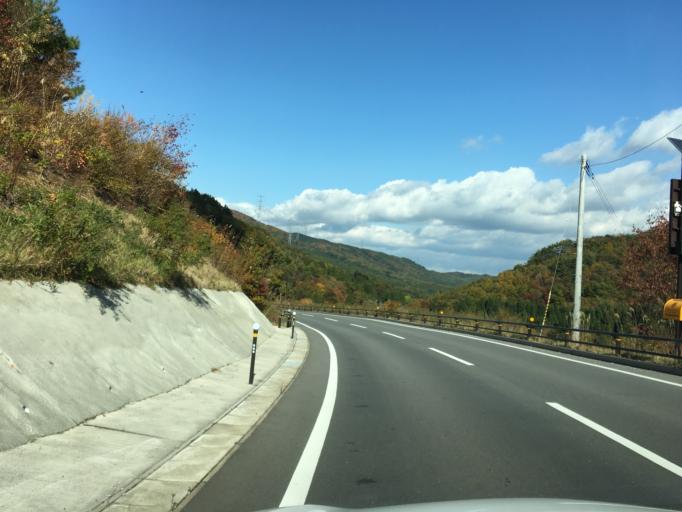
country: JP
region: Fukushima
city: Funehikimachi-funehiki
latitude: 37.2905
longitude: 140.7574
